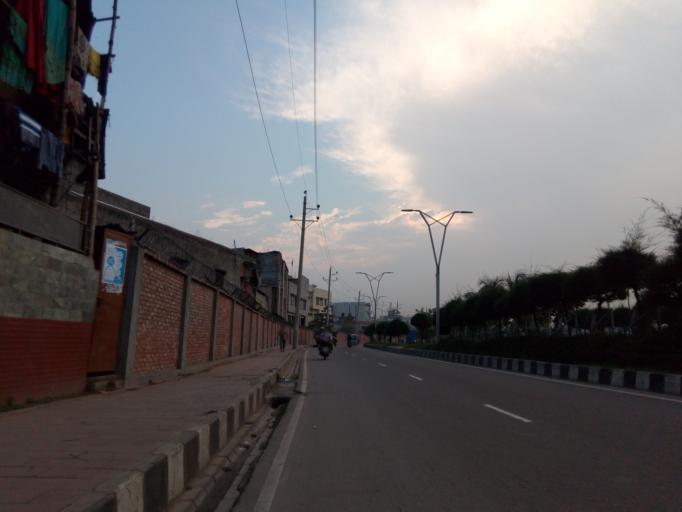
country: BD
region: Dhaka
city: Paltan
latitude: 23.7587
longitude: 90.4099
